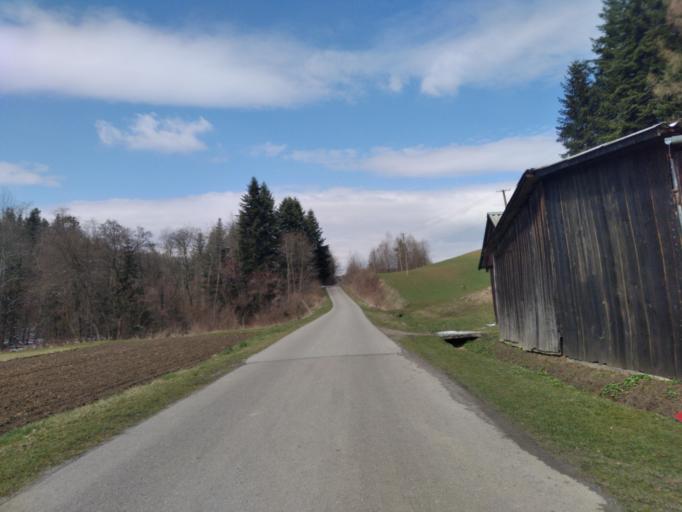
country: PL
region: Subcarpathian Voivodeship
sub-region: Powiat ropczycko-sedziszowski
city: Ropczyce
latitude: 50.0031
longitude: 21.5892
